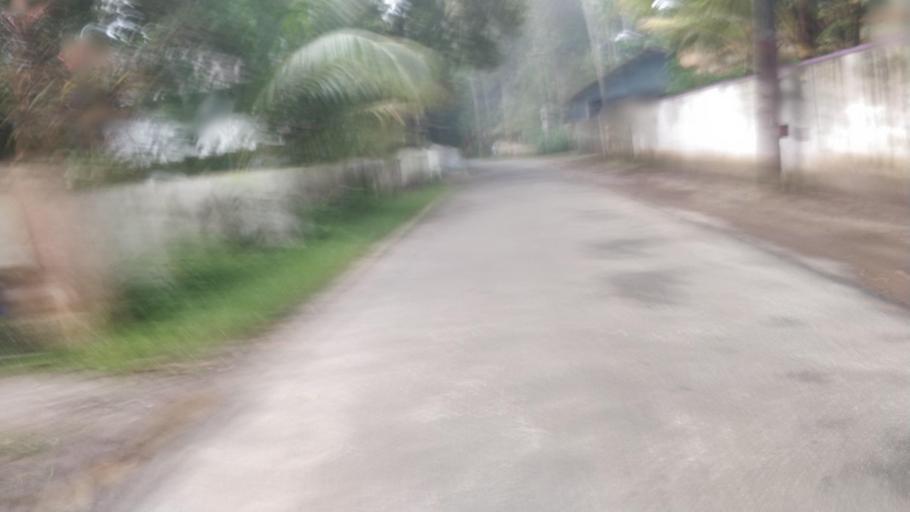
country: IN
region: Kerala
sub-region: Alappuzha
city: Vayalar
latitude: 9.7037
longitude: 76.3482
